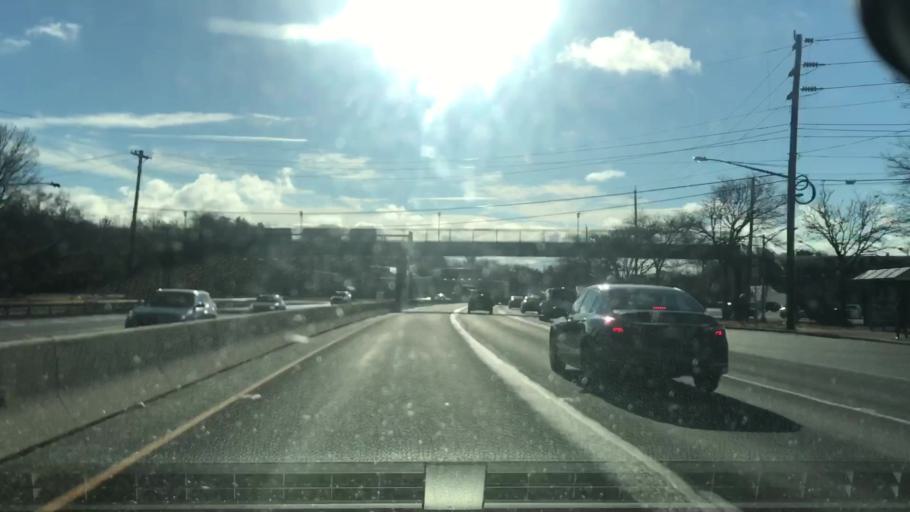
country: US
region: New Jersey
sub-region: Bergen County
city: Ho-Ho-Kus
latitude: 40.9796
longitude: -74.0841
